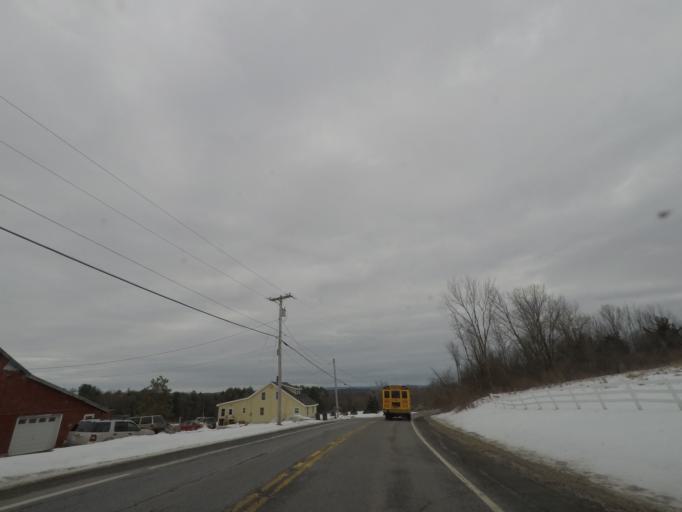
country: US
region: New York
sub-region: Saratoga County
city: Stillwater
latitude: 42.9526
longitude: -73.6666
